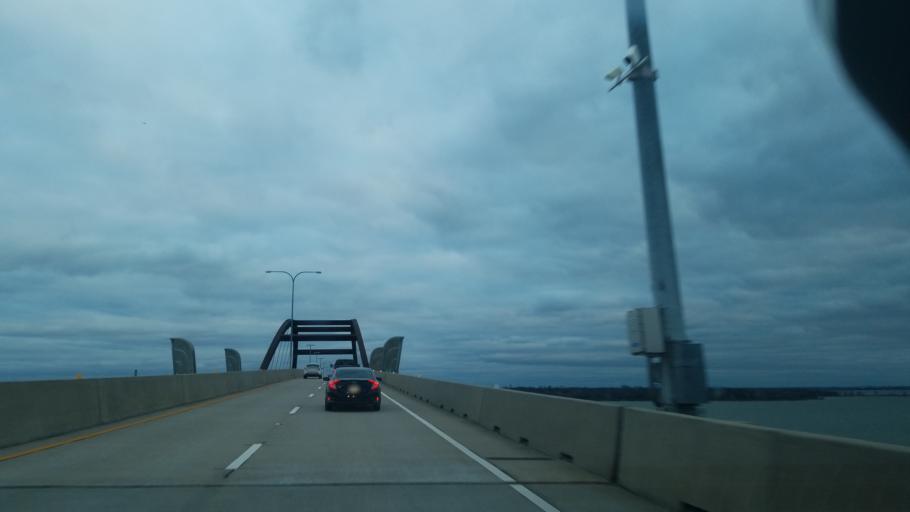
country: US
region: Texas
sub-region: Denton County
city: Lake Dallas
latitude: 33.1394
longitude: -97.0049
